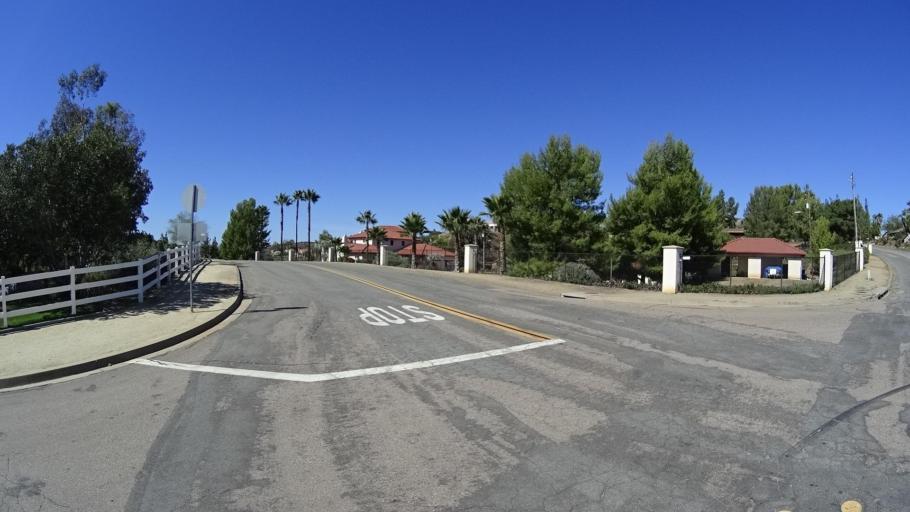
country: US
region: California
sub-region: San Diego County
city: Harbison Canyon
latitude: 32.8734
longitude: -116.8318
